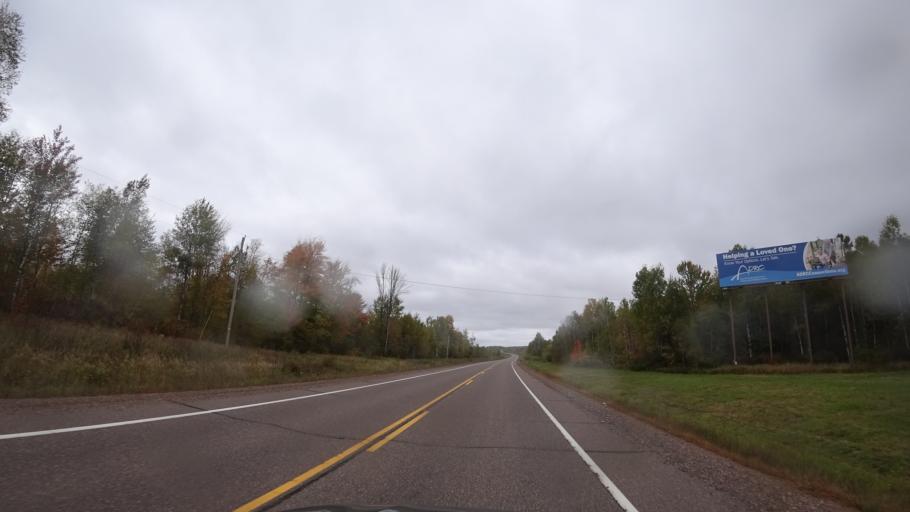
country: US
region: Wisconsin
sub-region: Rusk County
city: Ladysmith
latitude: 45.5797
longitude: -91.1122
